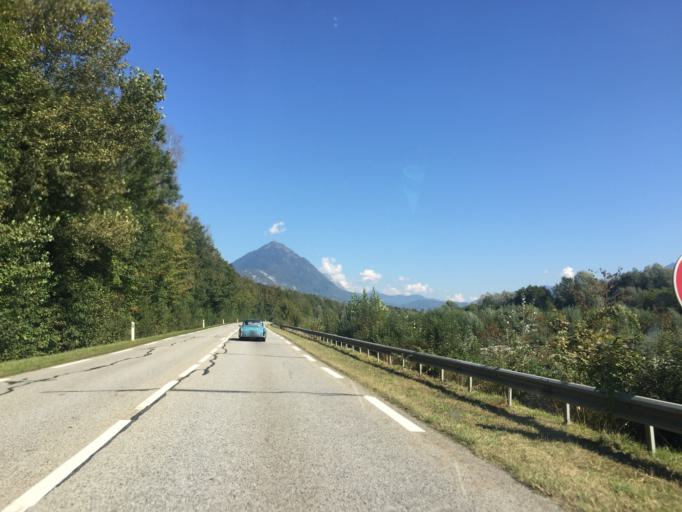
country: FR
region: Rhone-Alpes
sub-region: Departement de la Savoie
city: Gresy-sur-Isere
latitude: 45.6020
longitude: 6.2788
